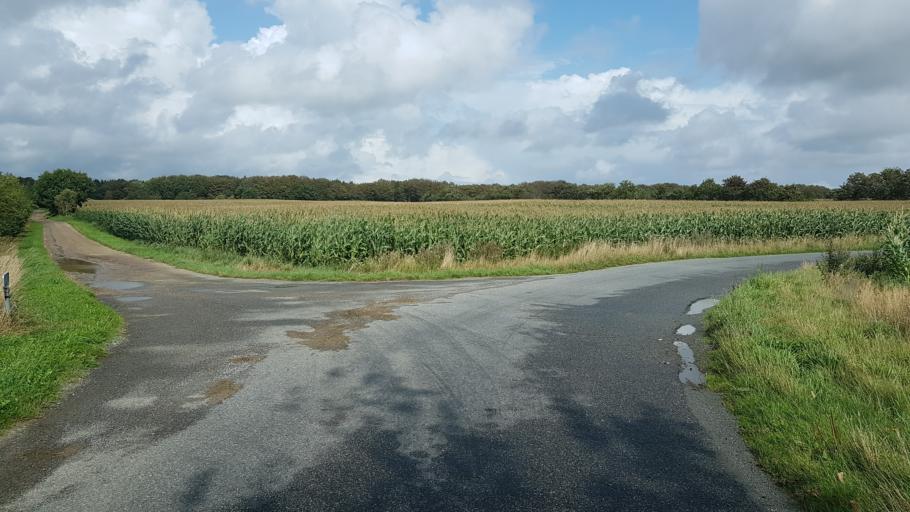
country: DK
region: South Denmark
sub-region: Vejen Kommune
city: Holsted
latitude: 55.4949
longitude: 8.9415
